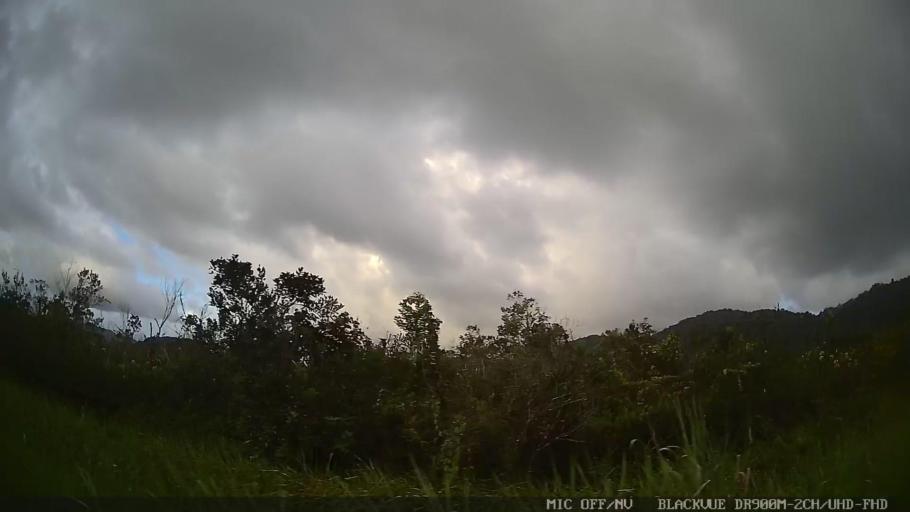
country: BR
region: Sao Paulo
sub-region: Itanhaem
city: Itanhaem
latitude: -24.1348
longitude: -46.7784
